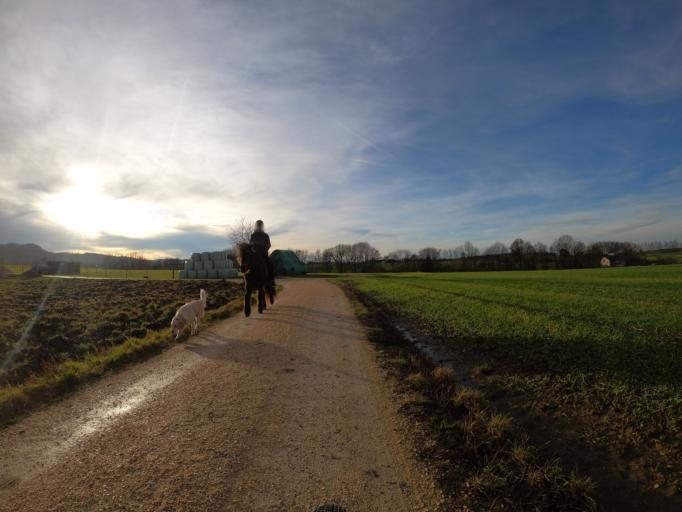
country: DE
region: Baden-Wuerttemberg
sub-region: Regierungsbezirk Stuttgart
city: Durnau
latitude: 48.6502
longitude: 9.6254
